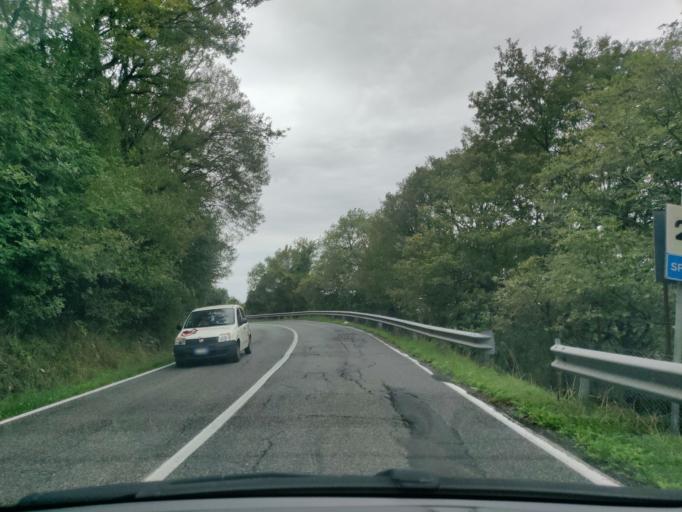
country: IT
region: Latium
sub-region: Citta metropolitana di Roma Capitale
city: Allumiere
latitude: 42.1452
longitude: 11.8905
